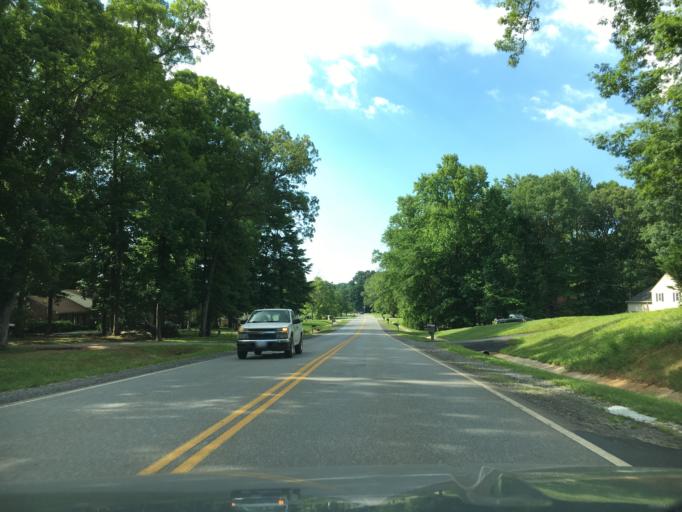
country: US
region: Virginia
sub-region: Bedford County
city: Forest
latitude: 37.3944
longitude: -79.2486
